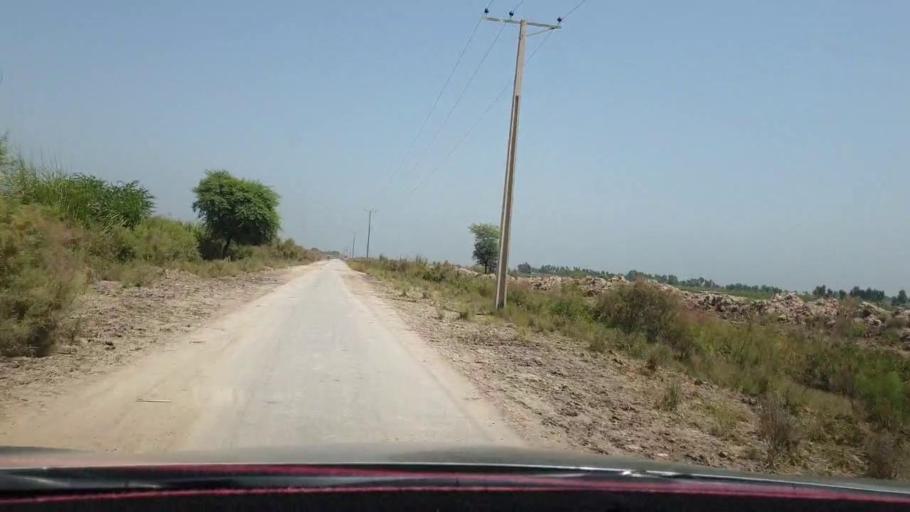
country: PK
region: Sindh
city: Warah
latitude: 27.4324
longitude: 67.7069
